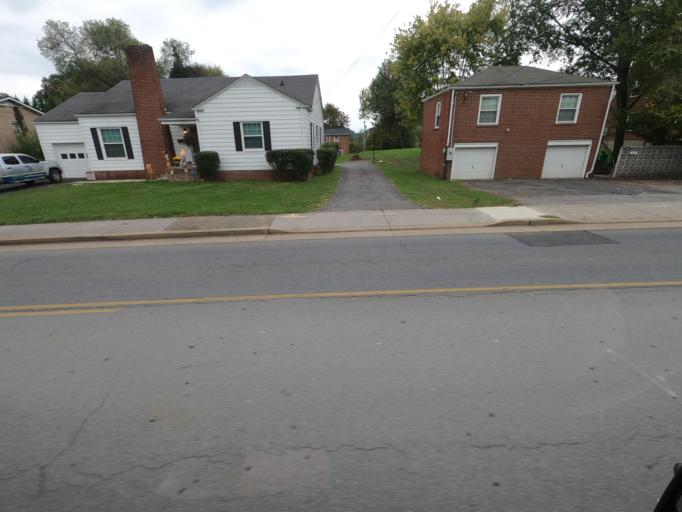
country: US
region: Tennessee
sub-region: Carter County
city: Elizabethton
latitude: 36.3456
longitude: -82.2251
